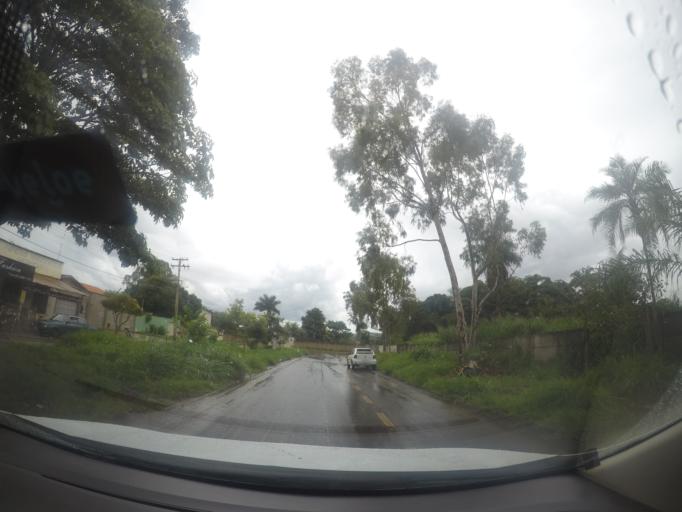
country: BR
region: Goias
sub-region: Trindade
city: Trindade
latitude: -16.6383
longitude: -49.4323
